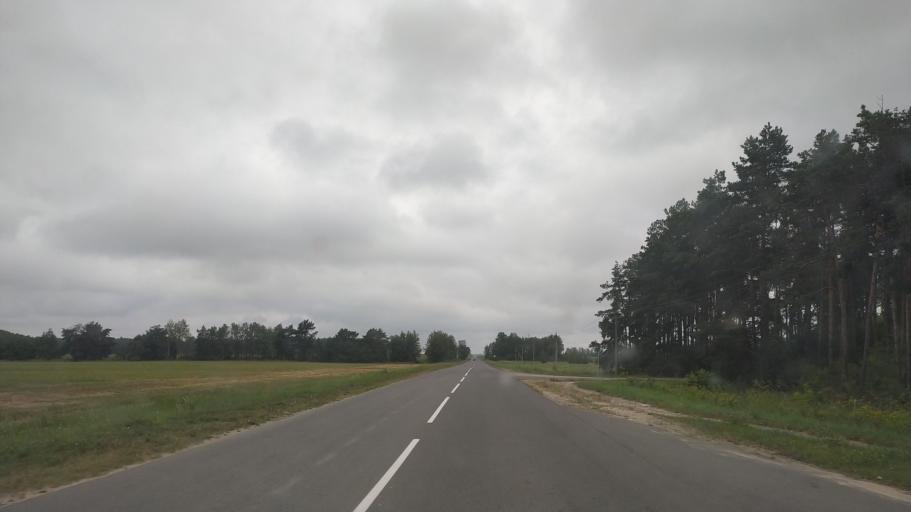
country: BY
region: Brest
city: Byaroza
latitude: 52.5586
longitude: 24.9130
